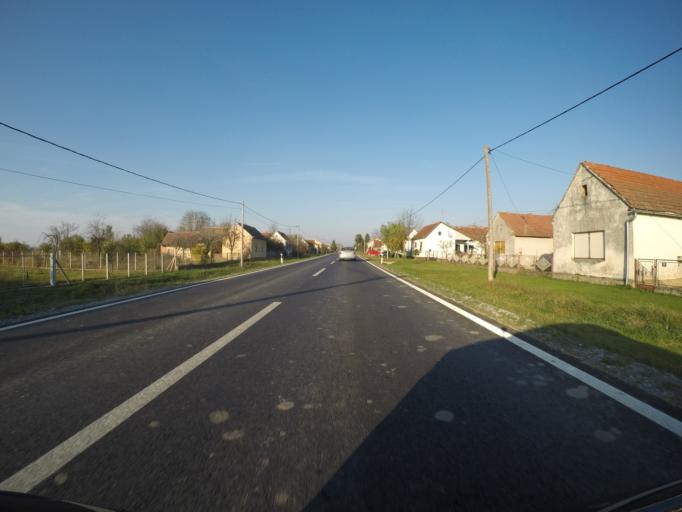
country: HU
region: Somogy
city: Barcs
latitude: 45.9244
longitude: 17.4544
